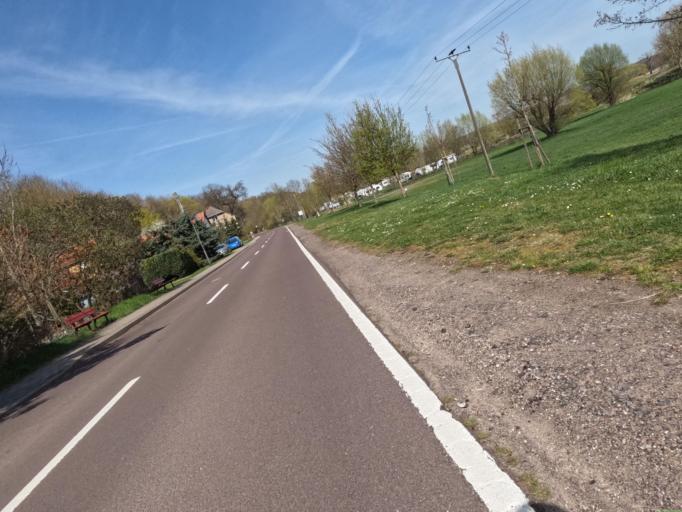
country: DE
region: Saxony-Anhalt
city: Beesenstedt
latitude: 51.5862
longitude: 11.7568
